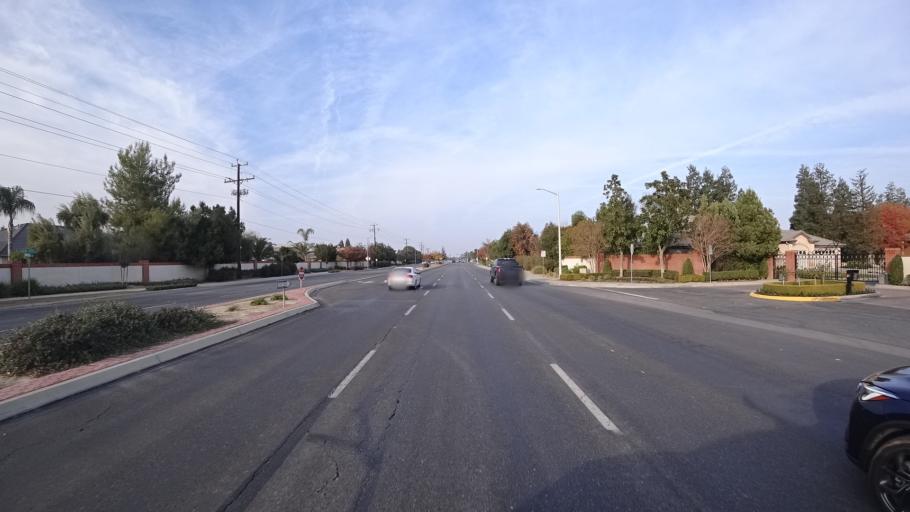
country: US
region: California
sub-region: Kern County
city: Greenacres
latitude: 35.3370
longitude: -119.1278
